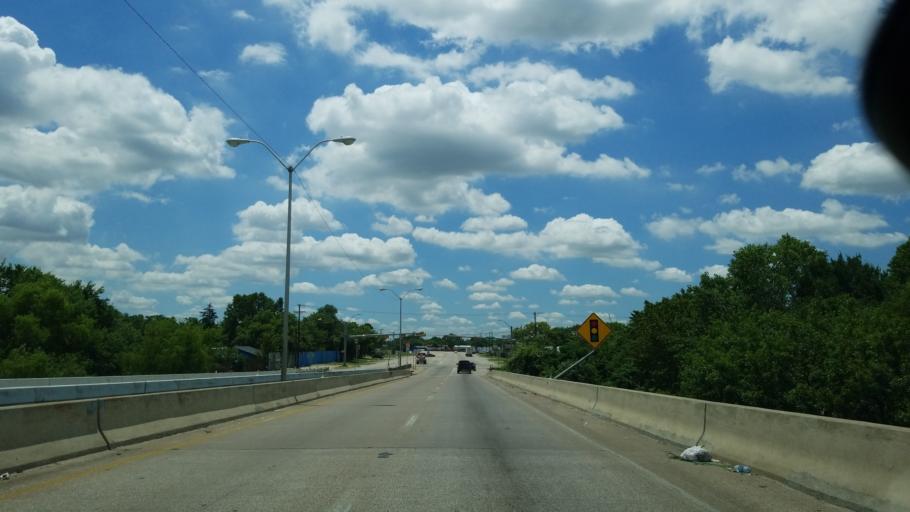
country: US
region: Texas
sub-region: Dallas County
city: Dallas
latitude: 32.7269
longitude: -96.7583
